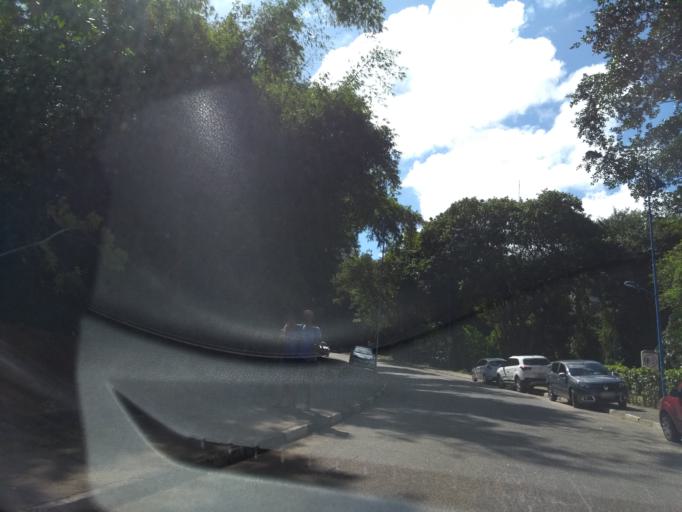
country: BR
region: Bahia
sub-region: Salvador
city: Salvador
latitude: -13.0001
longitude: -38.5087
